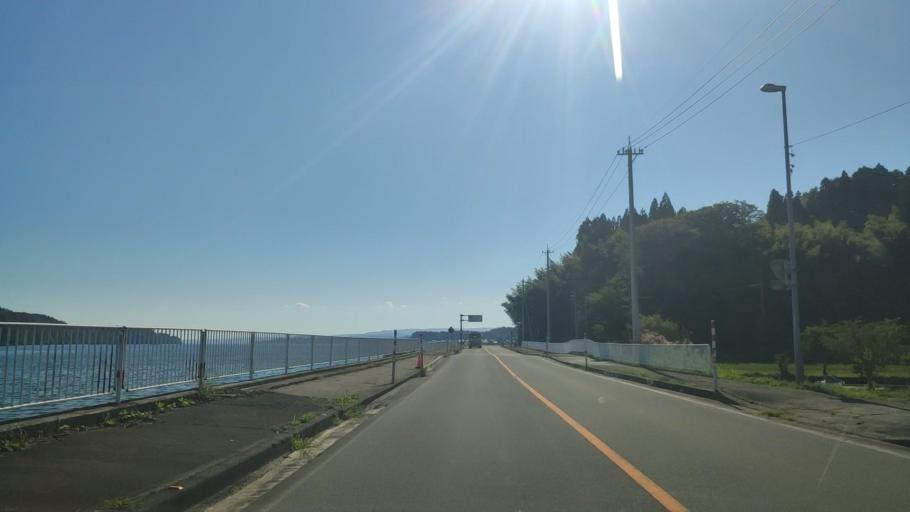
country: JP
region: Ishikawa
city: Nanao
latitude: 37.2363
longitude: 136.9595
